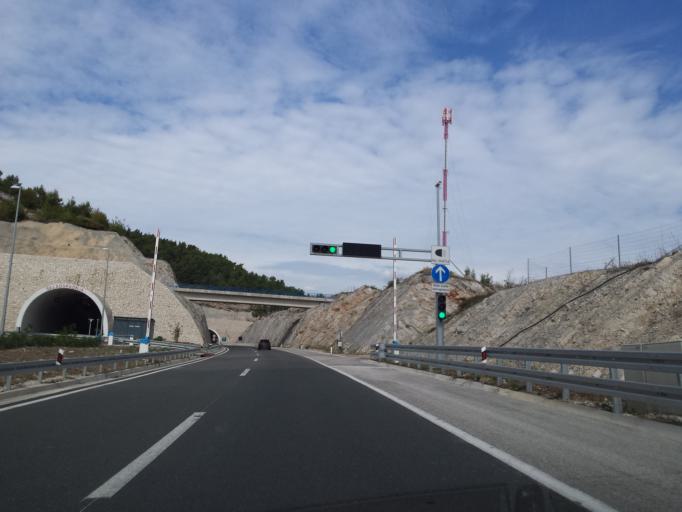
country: BA
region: Federation of Bosnia and Herzegovina
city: Vitina
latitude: 43.1604
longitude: 17.4751
